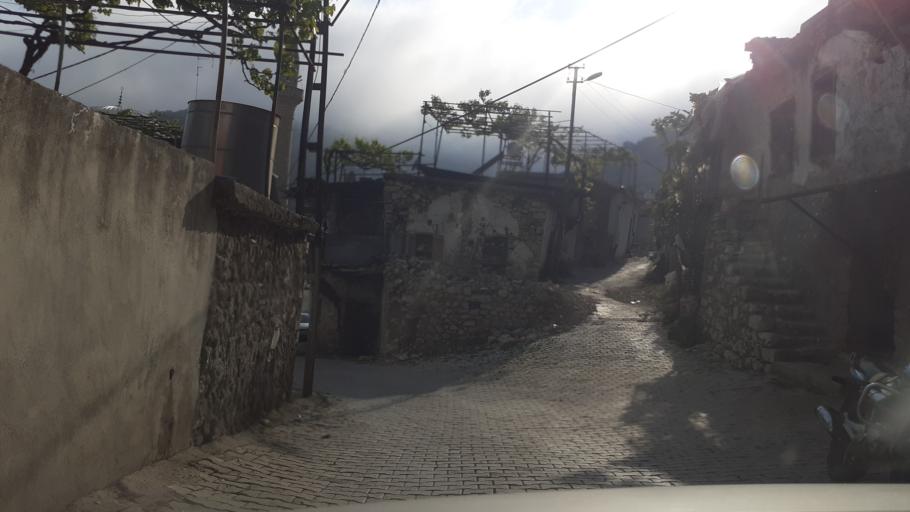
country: TR
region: Hatay
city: Yeditepe
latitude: 35.9686
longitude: 36.0153
